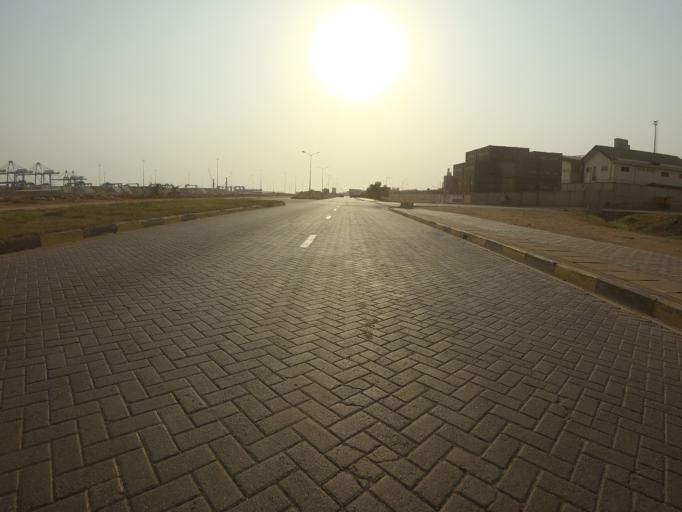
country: GH
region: Greater Accra
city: Tema
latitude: 5.6215
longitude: -0.0119
